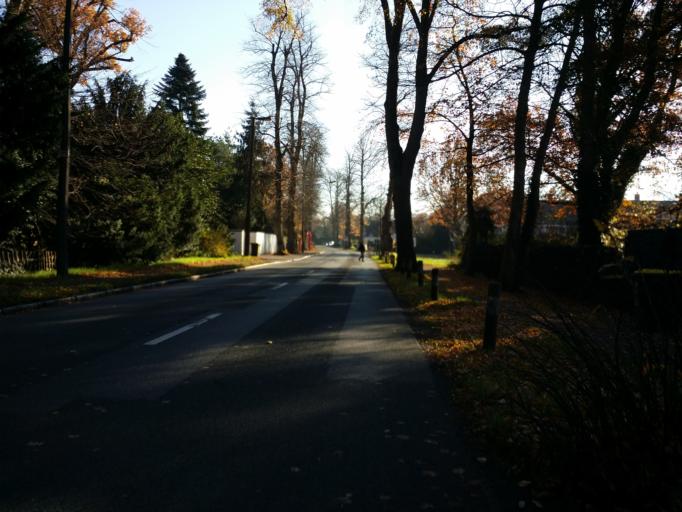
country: DE
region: Lower Saxony
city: Lilienthal
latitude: 53.0817
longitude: 8.9379
